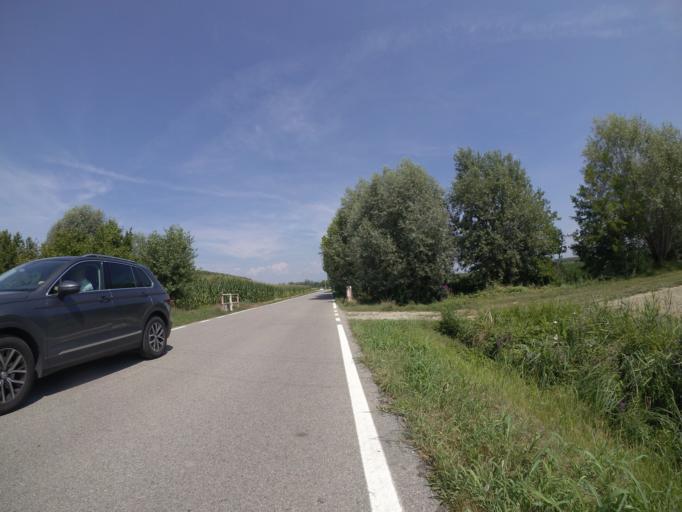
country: IT
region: Friuli Venezia Giulia
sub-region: Provincia di Udine
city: Camino al Tagliamento
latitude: 45.9174
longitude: 12.9647
